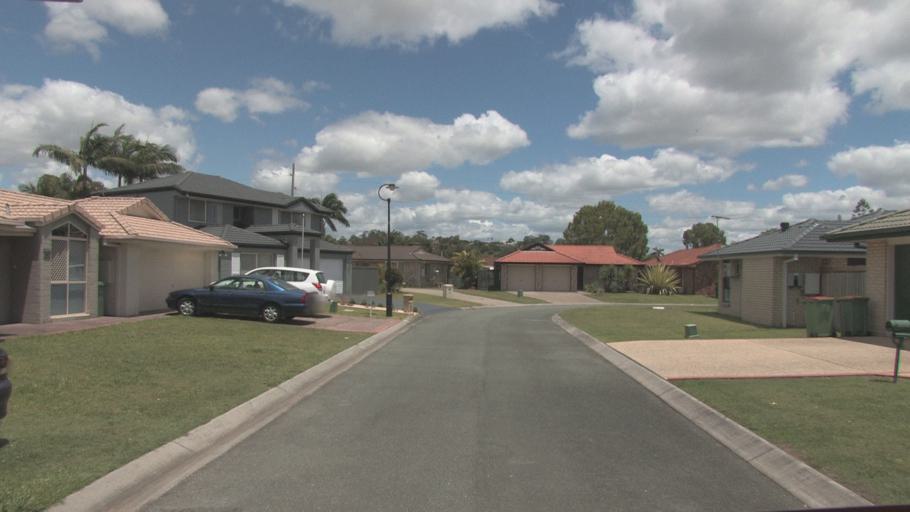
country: AU
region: Queensland
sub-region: Logan
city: Beenleigh
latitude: -27.6753
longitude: 153.2124
